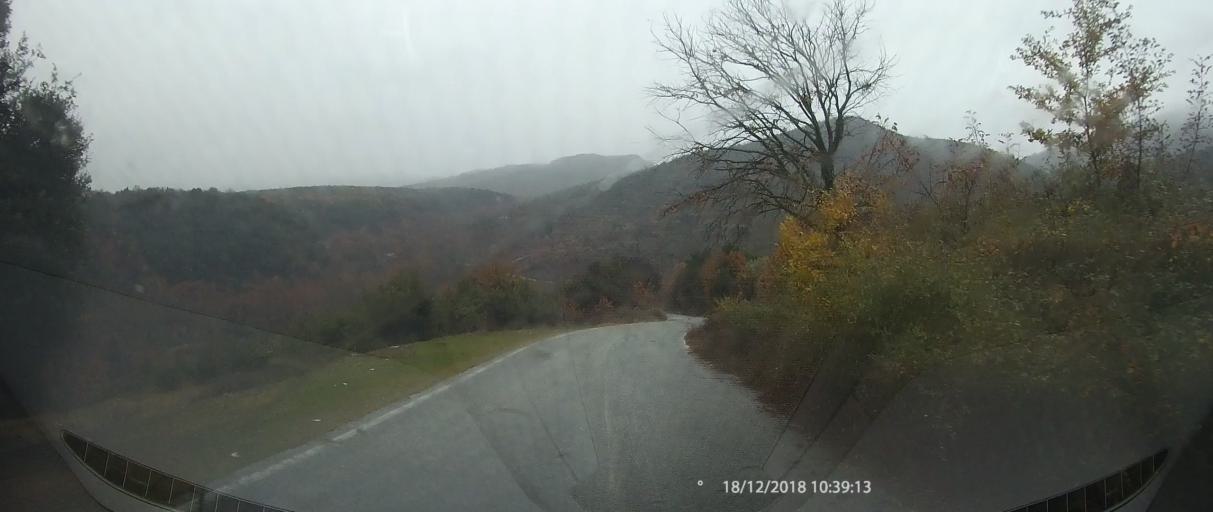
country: GR
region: Central Macedonia
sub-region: Nomos Pierias
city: Kato Milia
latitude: 40.2157
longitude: 22.3162
